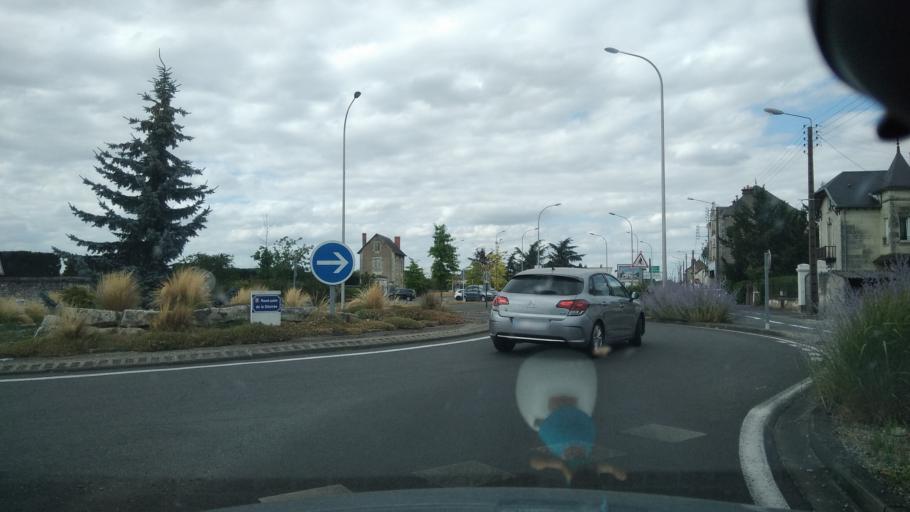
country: FR
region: Poitou-Charentes
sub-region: Departement de la Vienne
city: Antran
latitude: 46.8340
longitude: 0.5465
